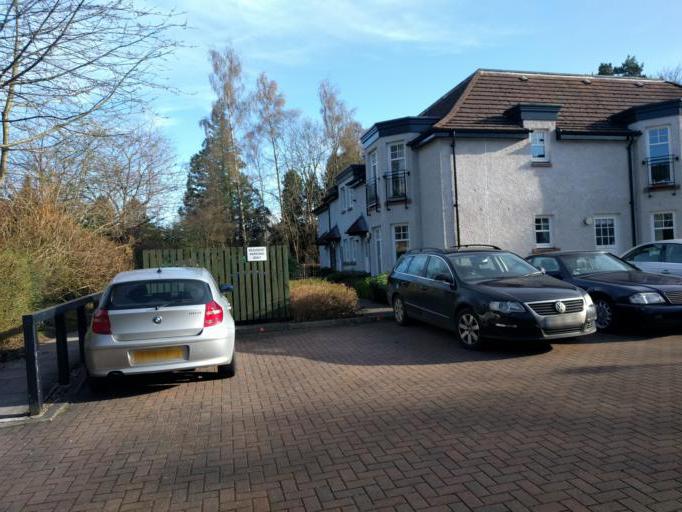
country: GB
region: Scotland
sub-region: Edinburgh
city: Balerno
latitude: 55.8880
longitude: -3.3422
